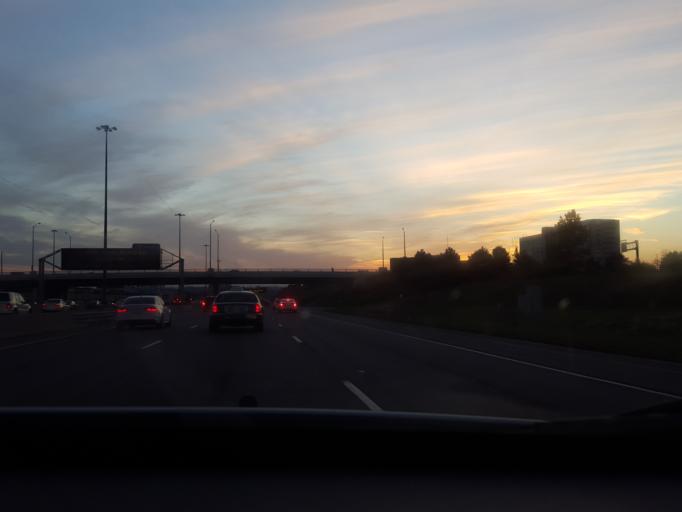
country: CA
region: Ontario
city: Toronto
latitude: 43.7234
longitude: -79.4792
